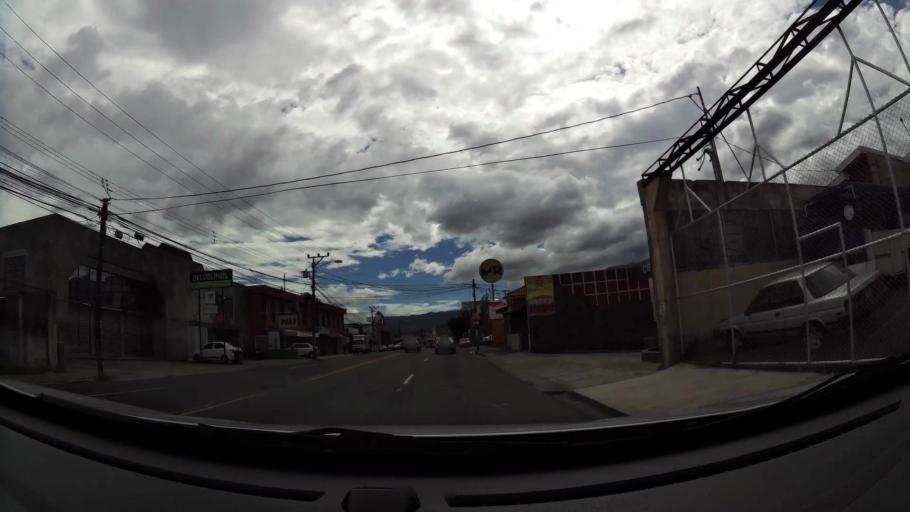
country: CR
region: San Jose
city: San Jose
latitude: 9.9142
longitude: -84.0848
